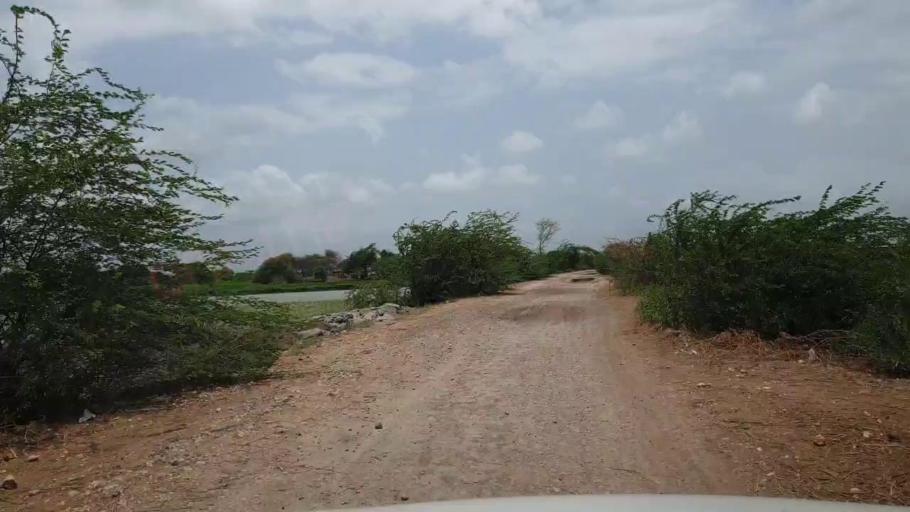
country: PK
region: Sindh
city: Kario
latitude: 24.7212
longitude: 68.5678
